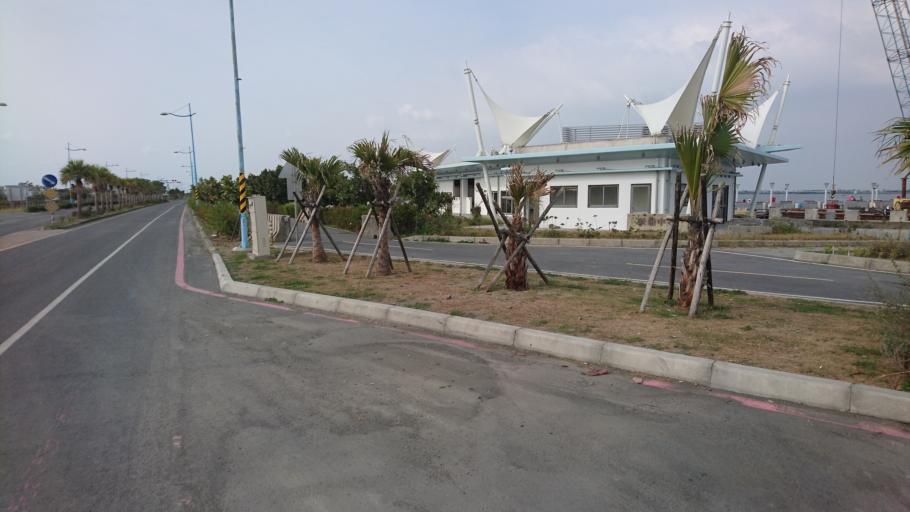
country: TW
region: Taiwan
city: Fengshan
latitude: 22.4379
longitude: 120.4744
